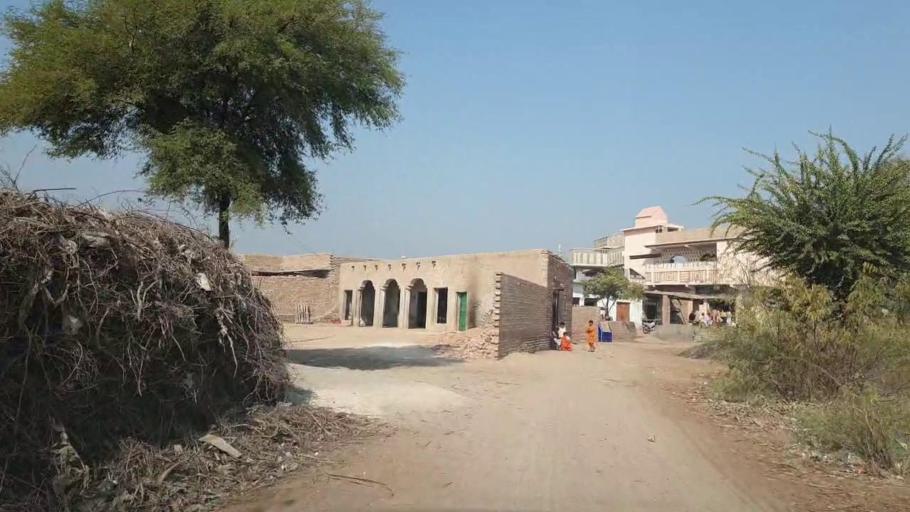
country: PK
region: Sindh
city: Matiari
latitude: 25.5546
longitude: 68.4815
